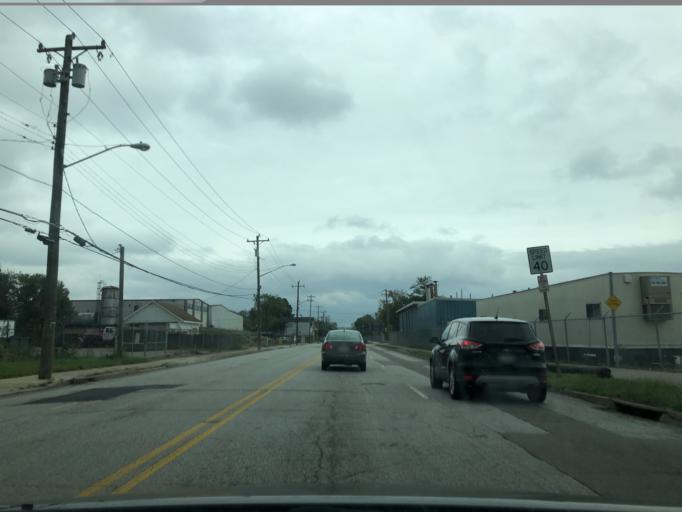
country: US
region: Kentucky
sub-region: Campbell County
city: Dayton
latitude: 39.1113
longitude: -84.4387
